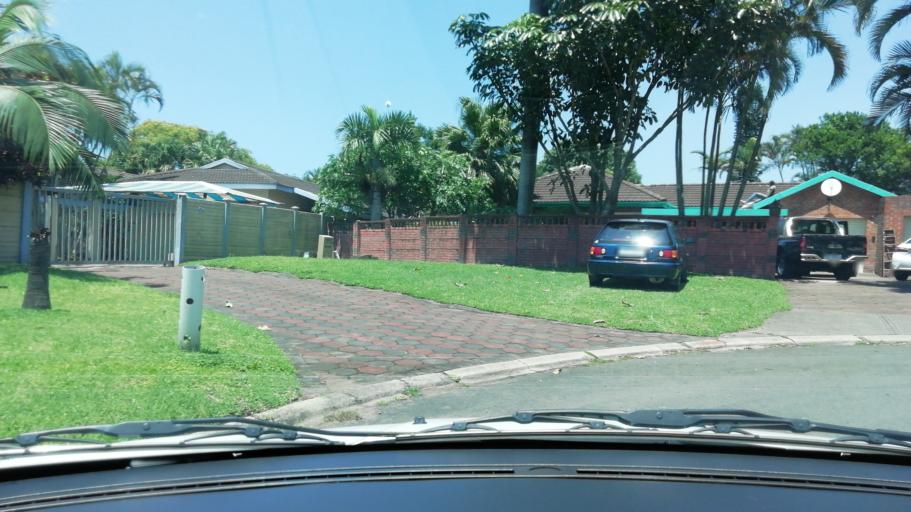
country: ZA
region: KwaZulu-Natal
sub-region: uThungulu District Municipality
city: Richards Bay
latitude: -28.7360
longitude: 32.0541
